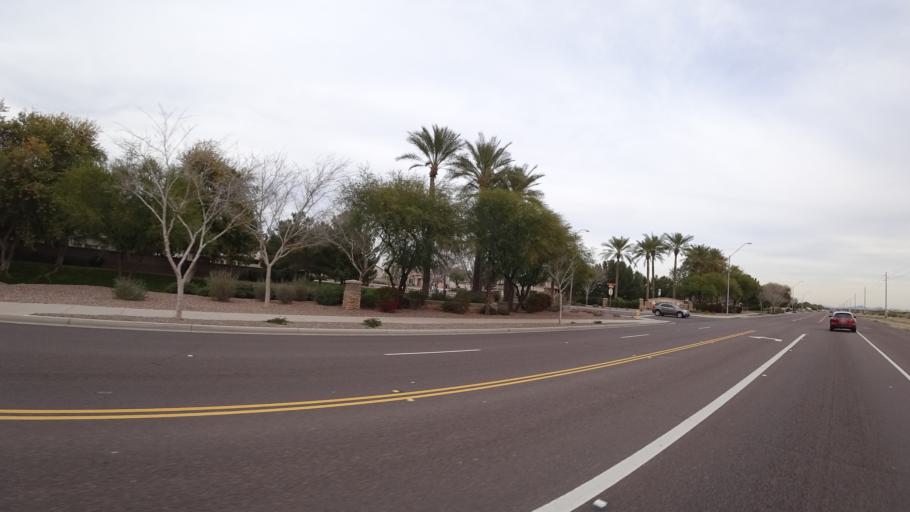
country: US
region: Arizona
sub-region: Maricopa County
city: Surprise
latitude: 33.6092
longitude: -112.3732
